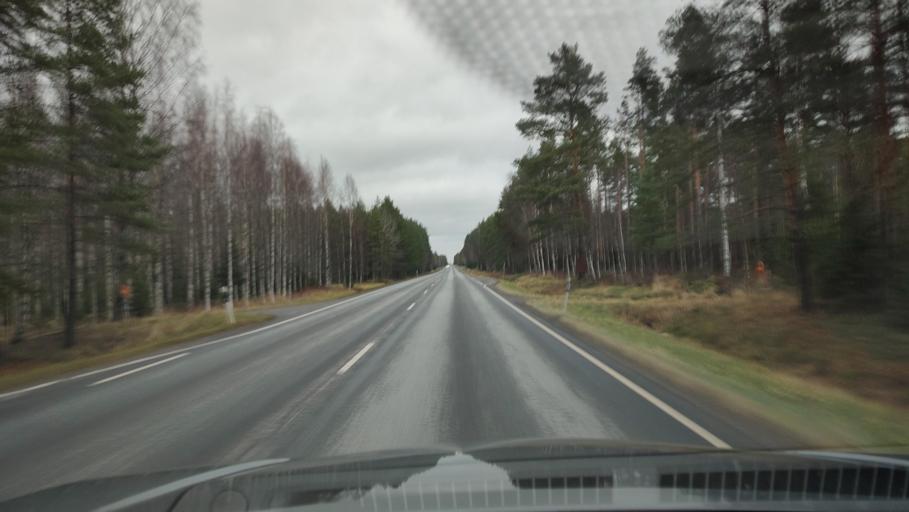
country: FI
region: Southern Ostrobothnia
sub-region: Seinaejoki
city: Kurikka
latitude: 62.5200
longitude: 22.3176
